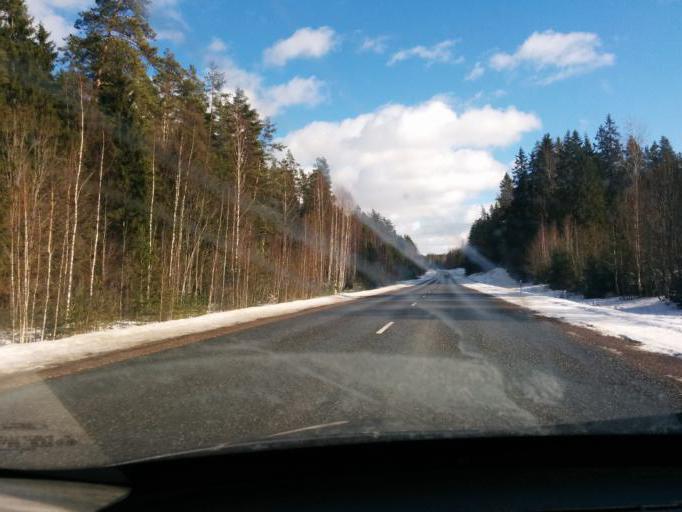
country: LV
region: Jaunpiebalga
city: Jaunpiebalga
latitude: 57.2377
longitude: 26.3017
